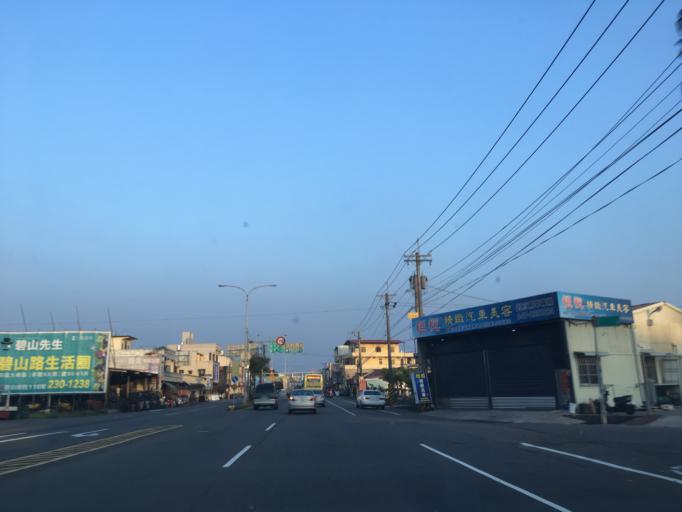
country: TW
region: Taiwan
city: Zhongxing New Village
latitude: 23.9976
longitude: 120.6620
